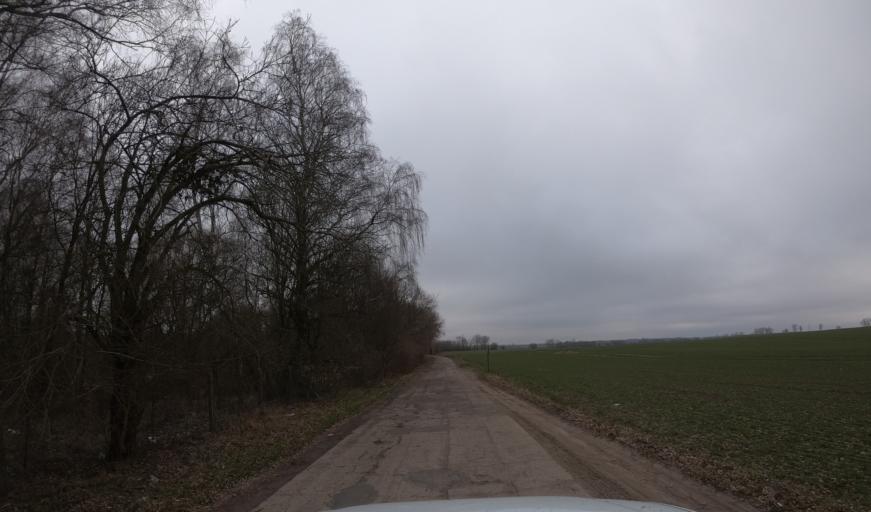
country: PL
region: West Pomeranian Voivodeship
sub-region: Powiat gryficki
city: Ploty
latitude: 53.8575
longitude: 15.2650
